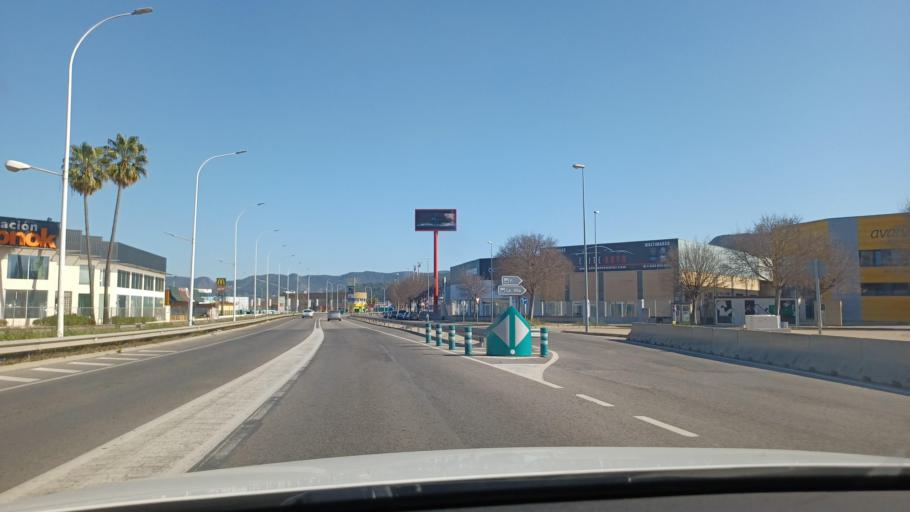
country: ES
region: Valencia
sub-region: Provincia de Valencia
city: Xativa
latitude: 38.9981
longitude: -0.5245
